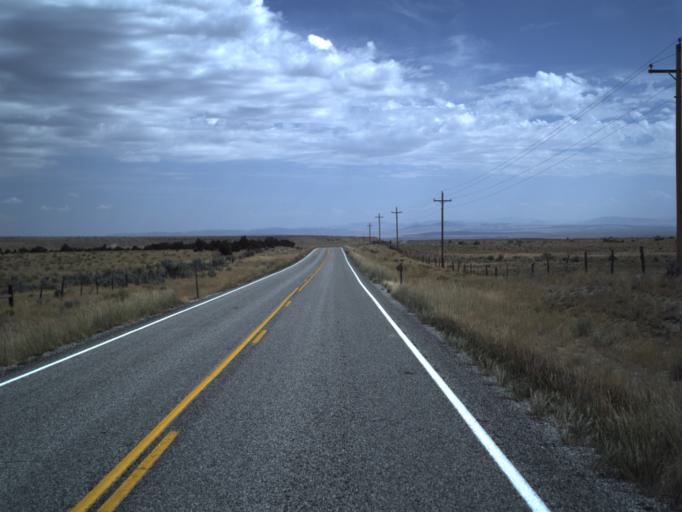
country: US
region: Idaho
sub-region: Cassia County
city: Burley
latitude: 41.8173
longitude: -113.2618
